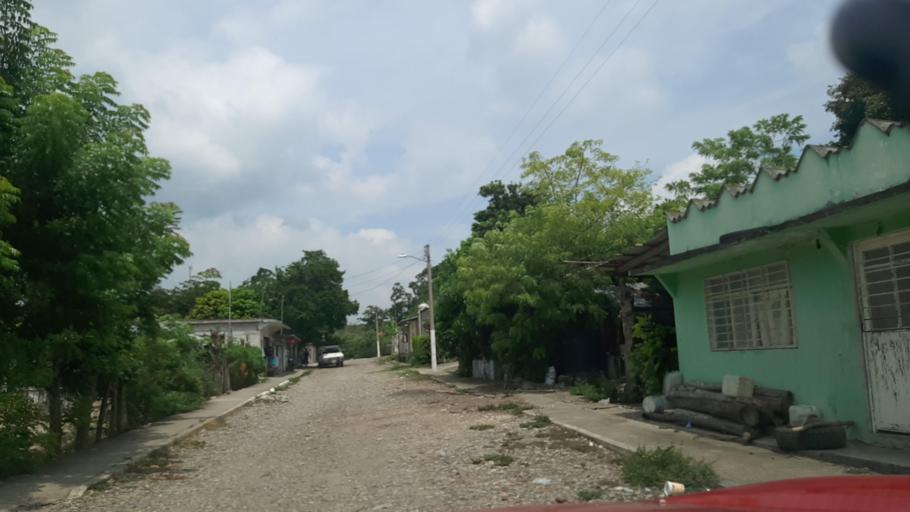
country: MX
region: Veracruz
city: Gutierrez Zamora
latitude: 20.4460
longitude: -97.1652
